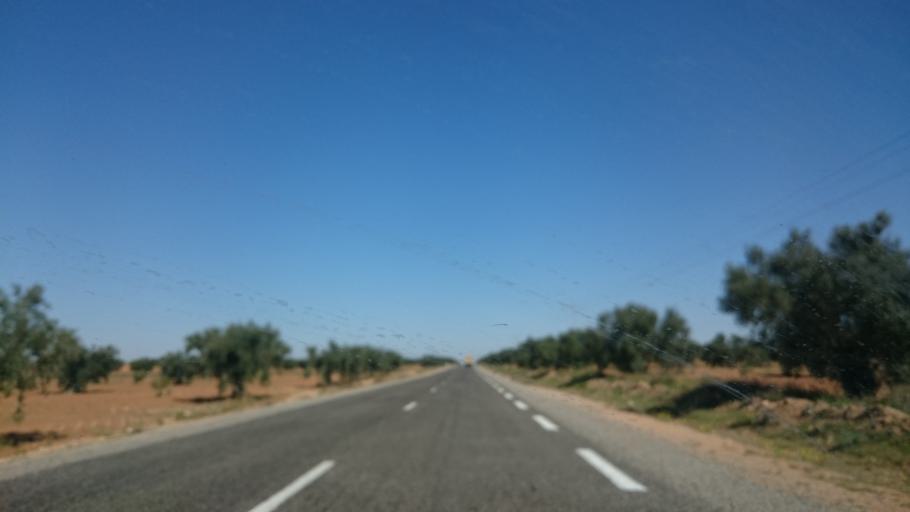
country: TN
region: Safaqis
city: Sfax
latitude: 34.8451
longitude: 10.4526
